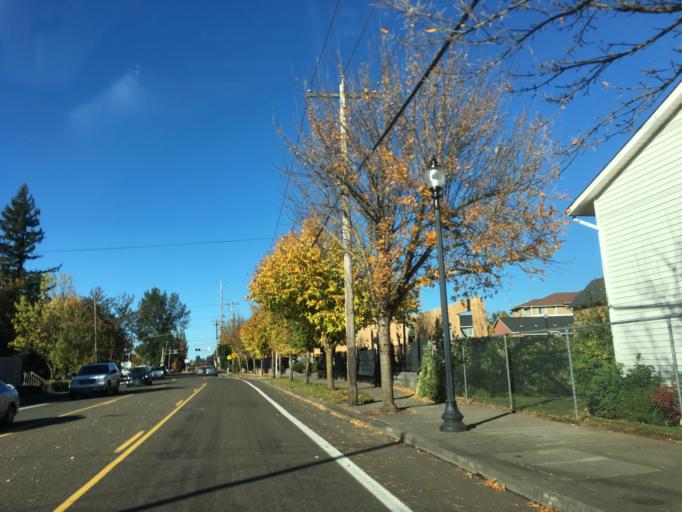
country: US
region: Oregon
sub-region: Multnomah County
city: Gresham
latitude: 45.5002
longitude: -122.4210
